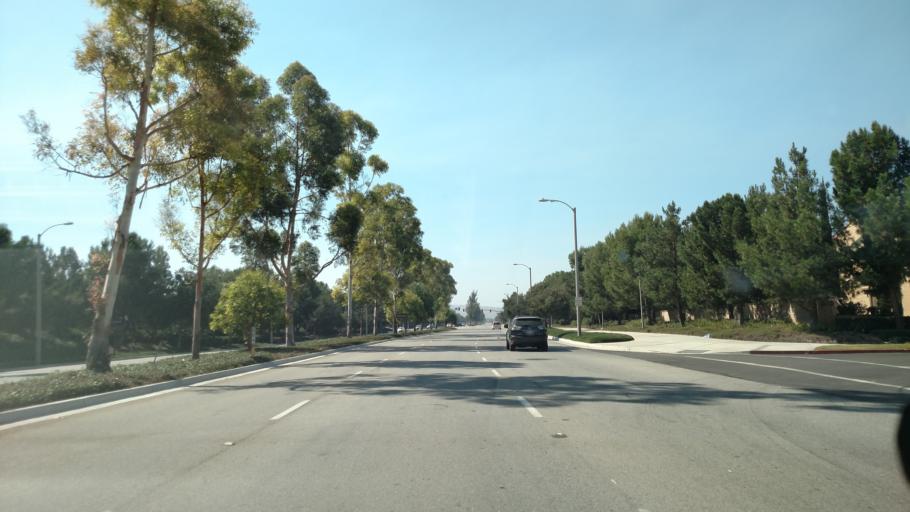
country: US
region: California
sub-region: Orange County
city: Lake Forest
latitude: 33.6950
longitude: -117.7413
